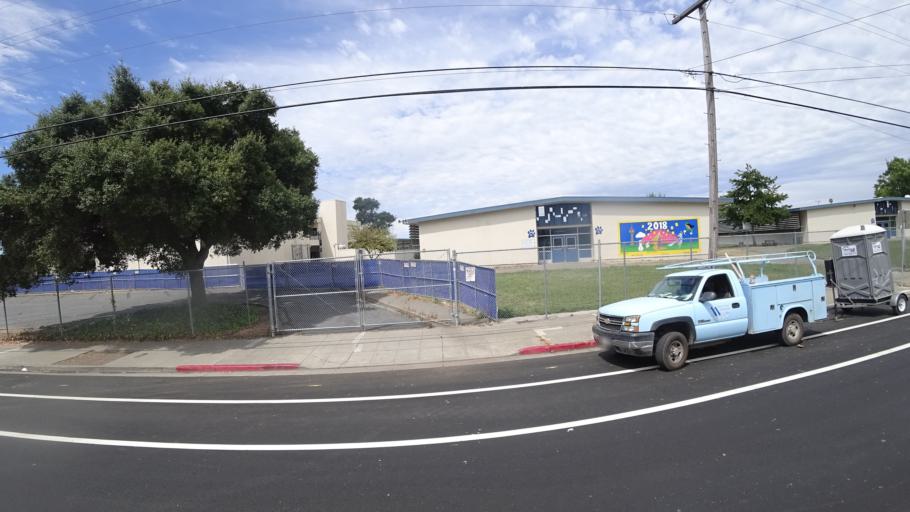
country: US
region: California
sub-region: Alameda County
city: Hayward
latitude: 37.6248
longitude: -122.0883
